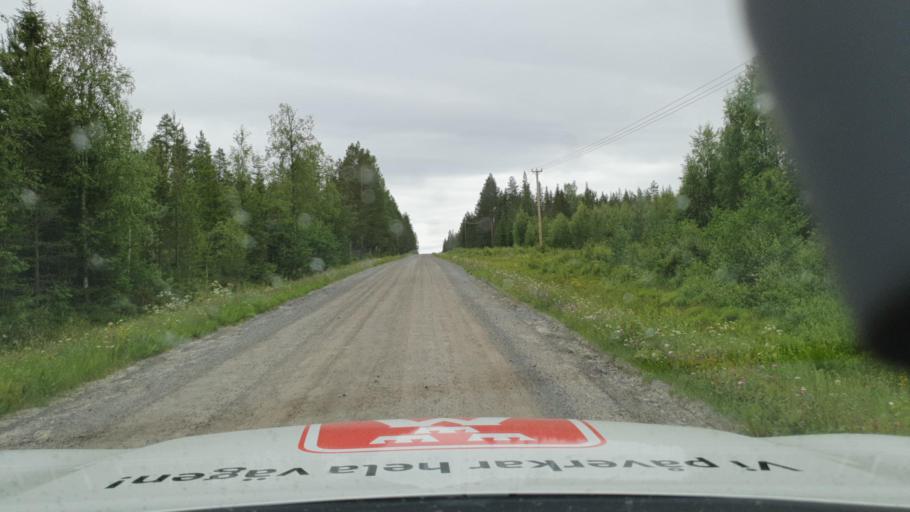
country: SE
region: Vaesterbotten
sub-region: Nordmalings Kommun
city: Nordmaling
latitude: 63.7407
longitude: 19.5028
